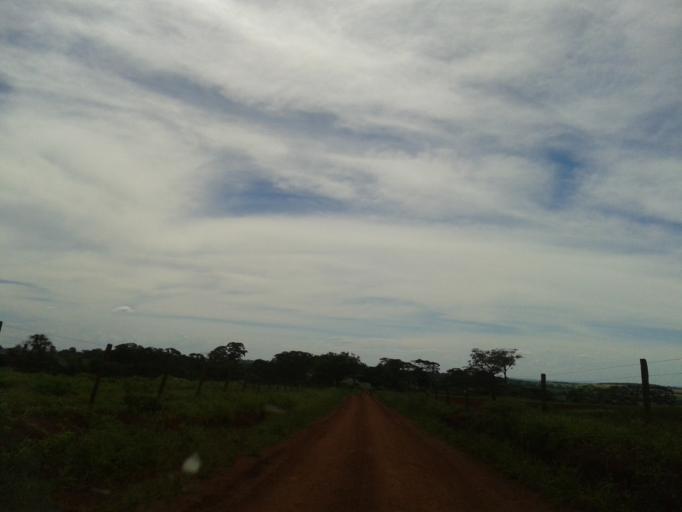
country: BR
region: Minas Gerais
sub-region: Capinopolis
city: Capinopolis
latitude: -18.7493
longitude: -49.8301
